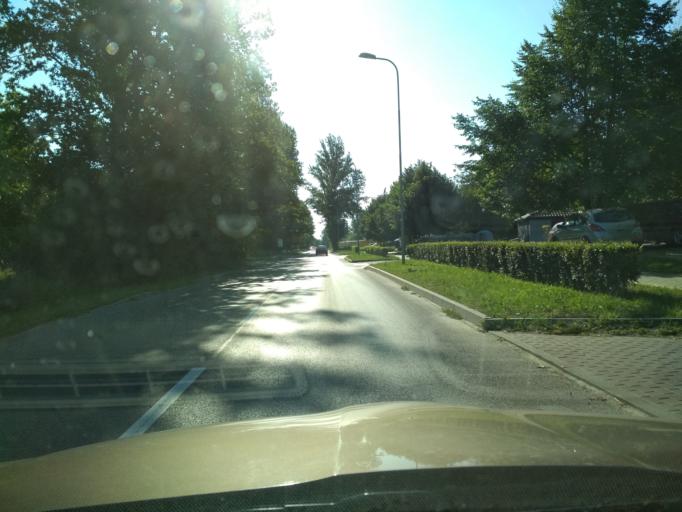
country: PL
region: Subcarpathian Voivodeship
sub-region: Rzeszow
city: Rzeszow
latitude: 50.0632
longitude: 21.9811
